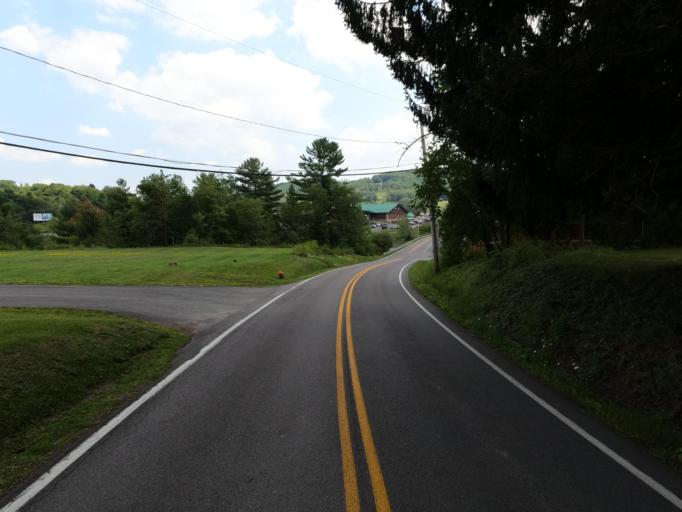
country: US
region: Maryland
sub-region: Garrett County
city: Oakland
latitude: 39.5592
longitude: -79.3555
